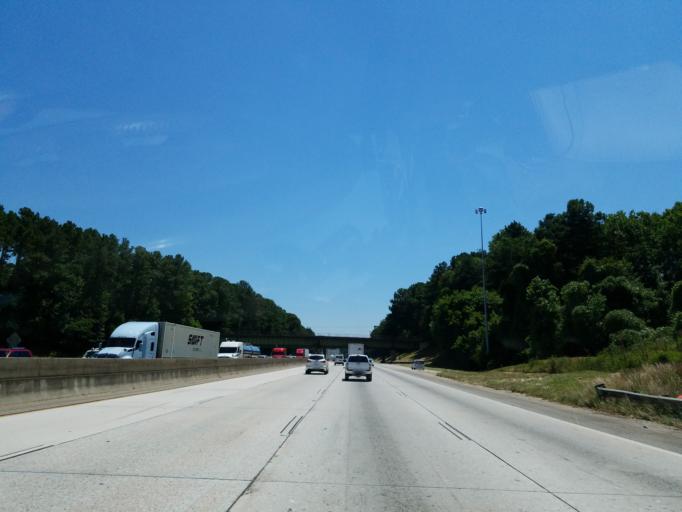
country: US
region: Georgia
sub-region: Fulton County
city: East Point
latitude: 33.7527
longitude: -84.4959
